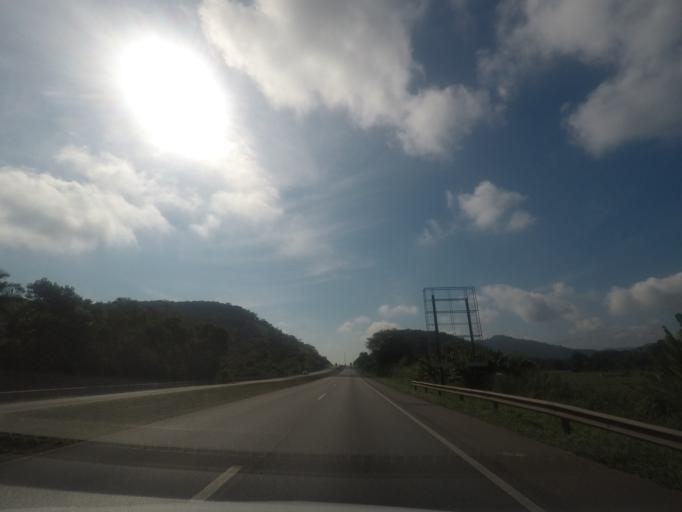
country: BR
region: Parana
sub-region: Antonina
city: Antonina
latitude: -25.5353
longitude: -48.7620
